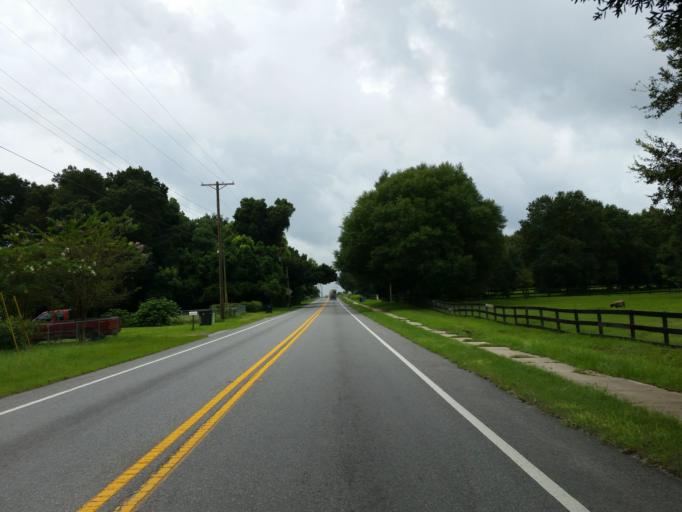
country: US
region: Florida
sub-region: Hillsborough County
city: Thonotosassa
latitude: 28.0502
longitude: -82.3027
